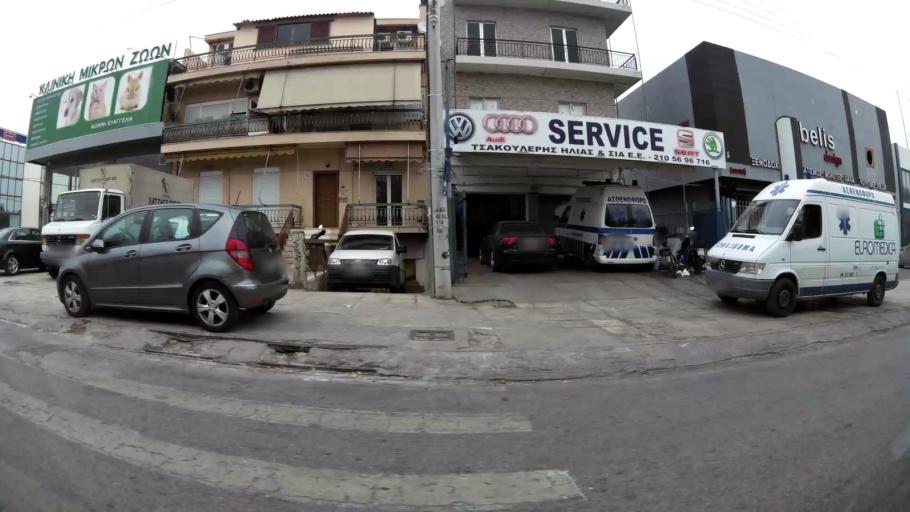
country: GR
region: Attica
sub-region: Nomarchia Athinas
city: Chaidari
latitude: 38.0053
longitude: 23.6768
